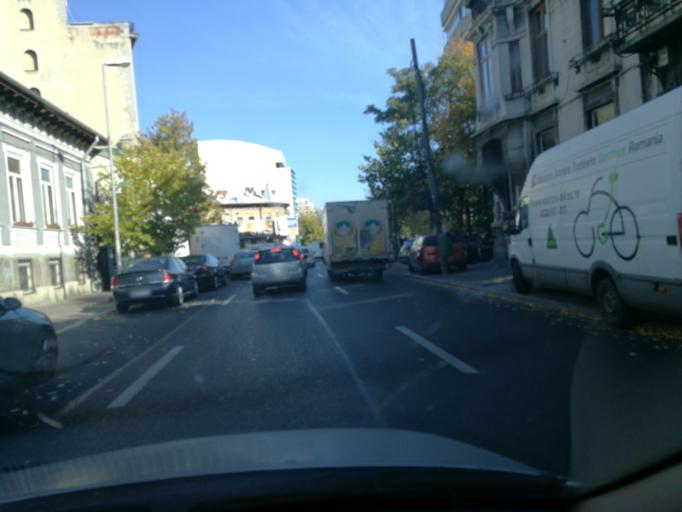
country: RO
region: Bucuresti
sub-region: Municipiul Bucuresti
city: Bucuresti
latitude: 44.4400
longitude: 26.0873
